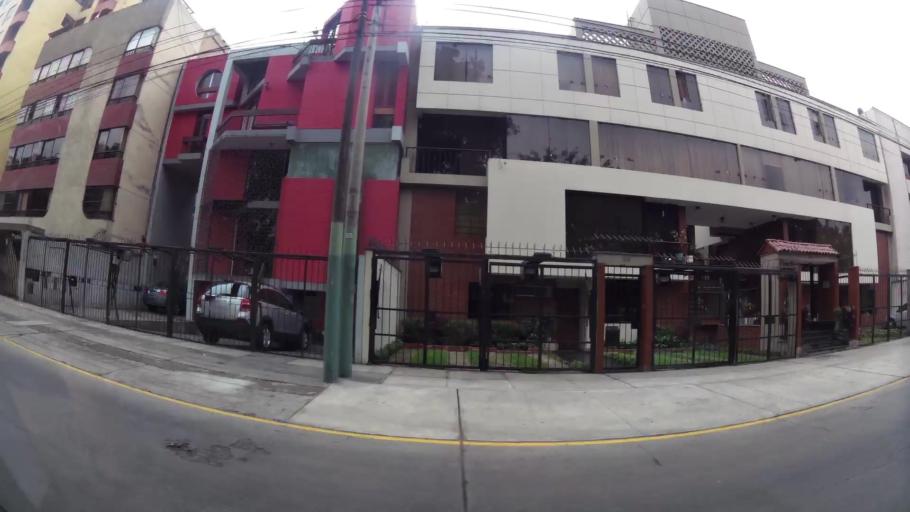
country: PE
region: Lima
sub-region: Lima
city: San Luis
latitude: -12.1018
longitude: -76.9918
